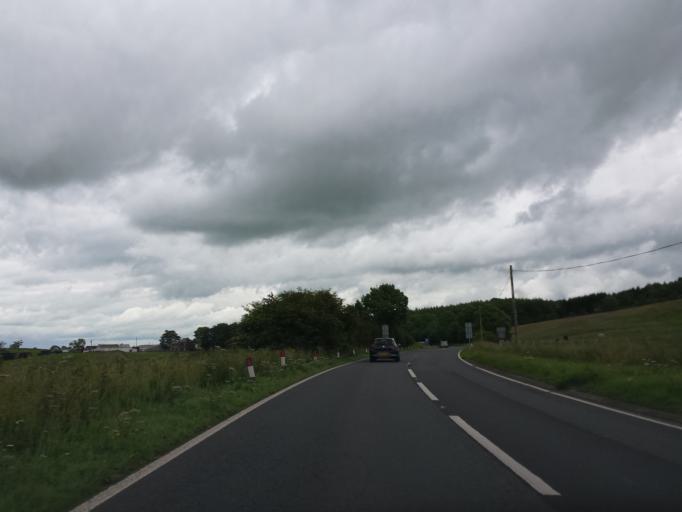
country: GB
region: Scotland
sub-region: Dumfries and Galloway
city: Dalbeattie
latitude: 55.0379
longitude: -3.8236
